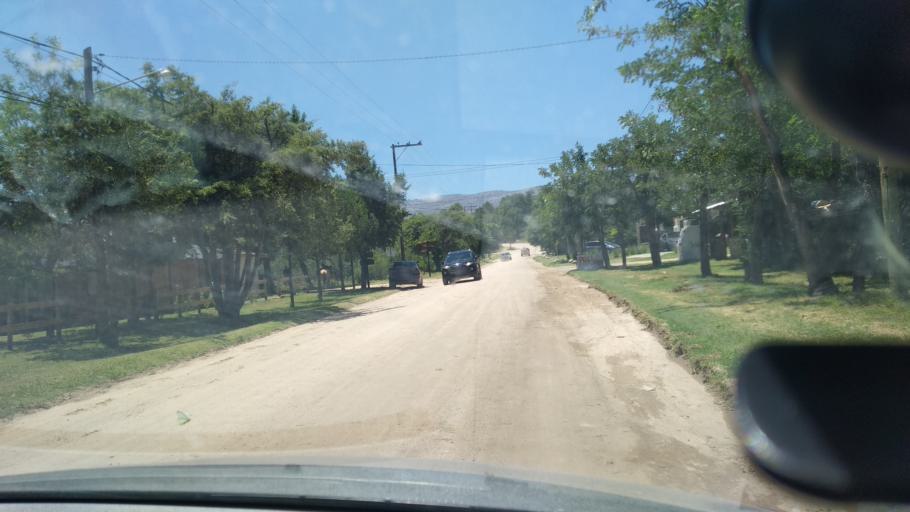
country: AR
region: Cordoba
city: Mina Clavero
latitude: -31.7975
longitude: -65.0105
